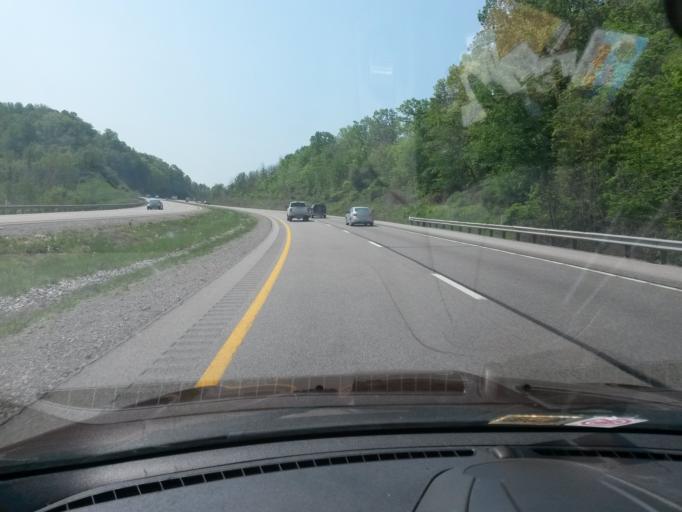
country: US
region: West Virginia
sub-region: Lewis County
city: Weston
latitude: 38.9535
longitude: -80.5348
